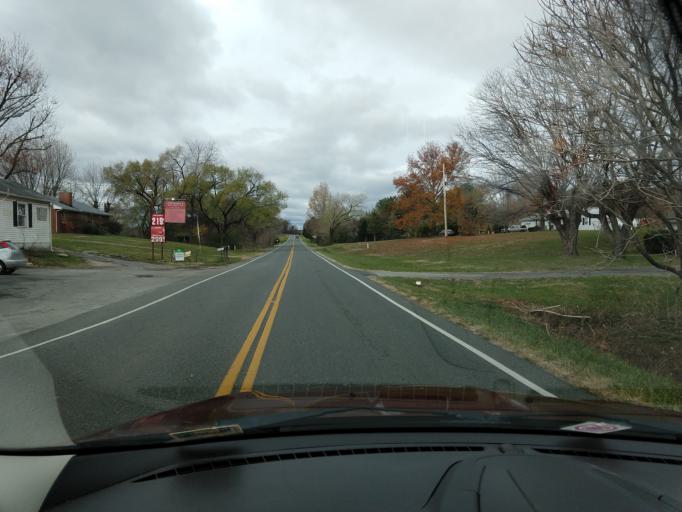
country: US
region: Virginia
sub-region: Franklin County
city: North Shore
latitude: 37.2448
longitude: -79.6819
